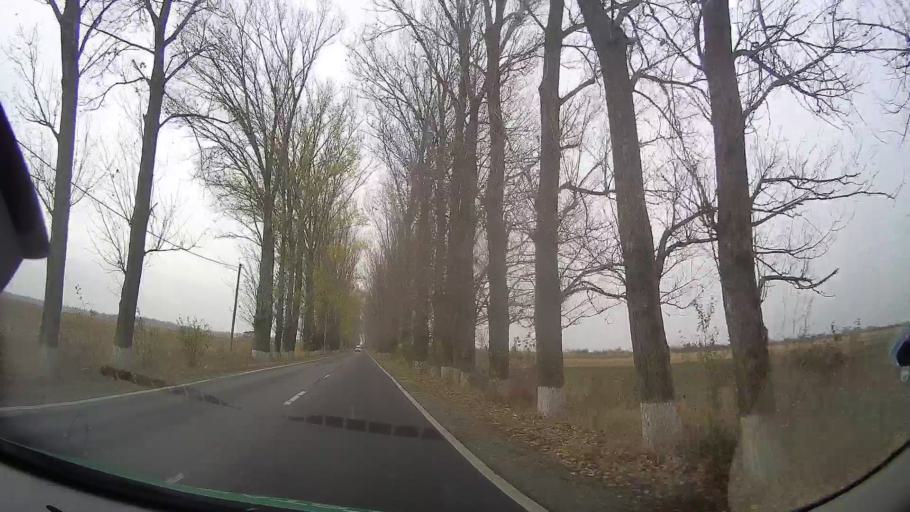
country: RO
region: Ilfov
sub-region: Comuna Gruiu
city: Silistea Snagovului
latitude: 44.7432
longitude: 26.2046
